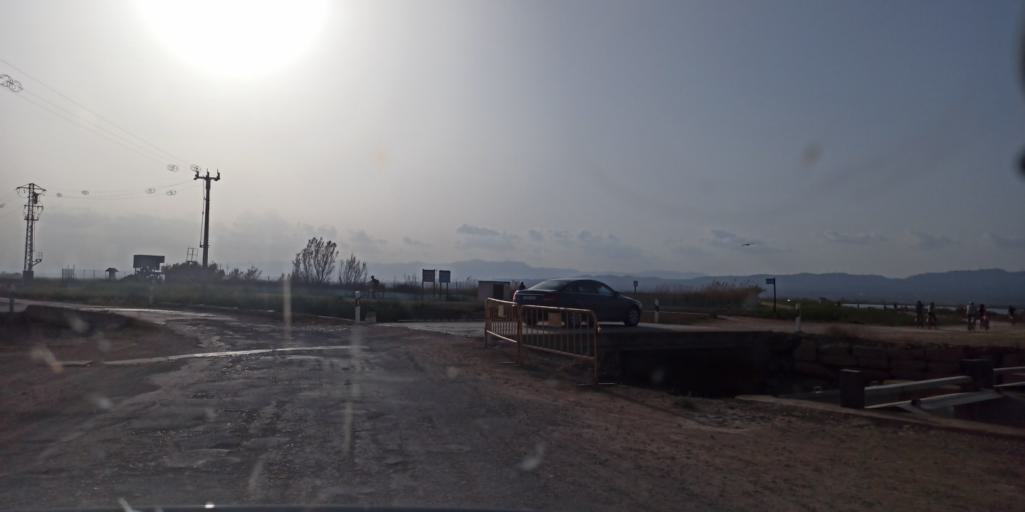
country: ES
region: Catalonia
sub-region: Provincia de Tarragona
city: L'Ampolla
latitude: 40.7666
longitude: 0.7371
